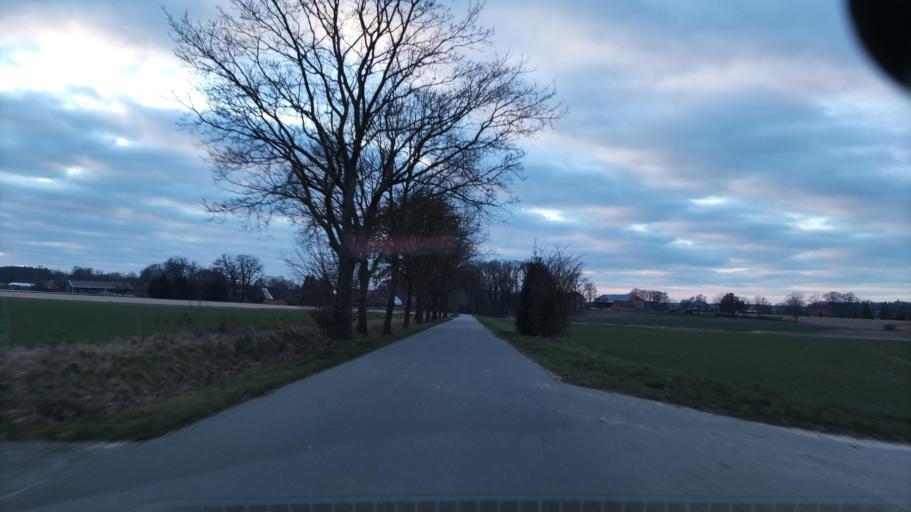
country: DE
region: Lower Saxony
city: Natendorf
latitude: 53.0554
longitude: 10.4622
